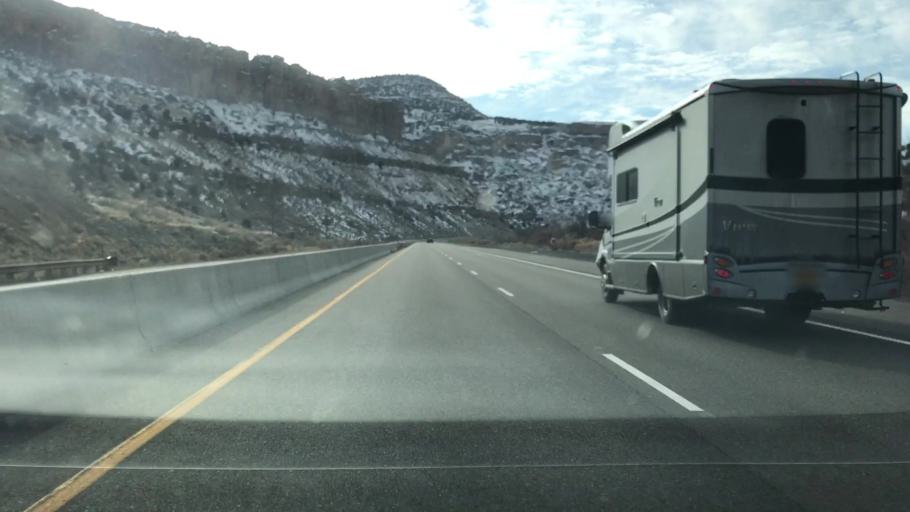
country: US
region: Colorado
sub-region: Mesa County
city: Palisade
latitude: 39.2157
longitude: -108.2565
